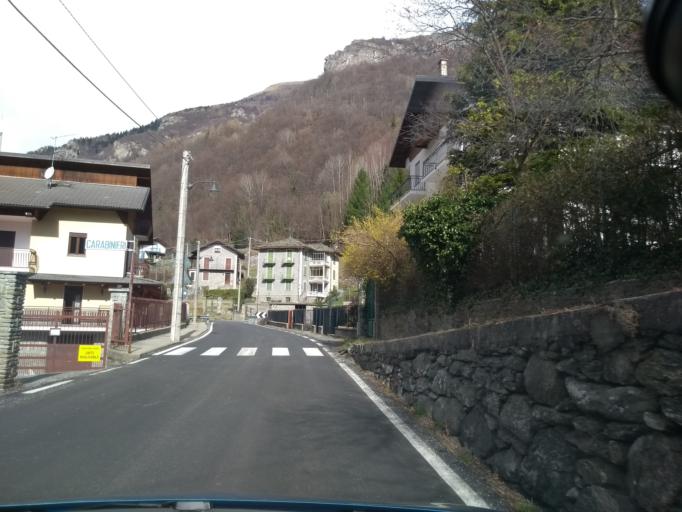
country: IT
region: Piedmont
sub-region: Provincia di Torino
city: Chialamberto
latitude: 45.3644
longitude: 7.3399
